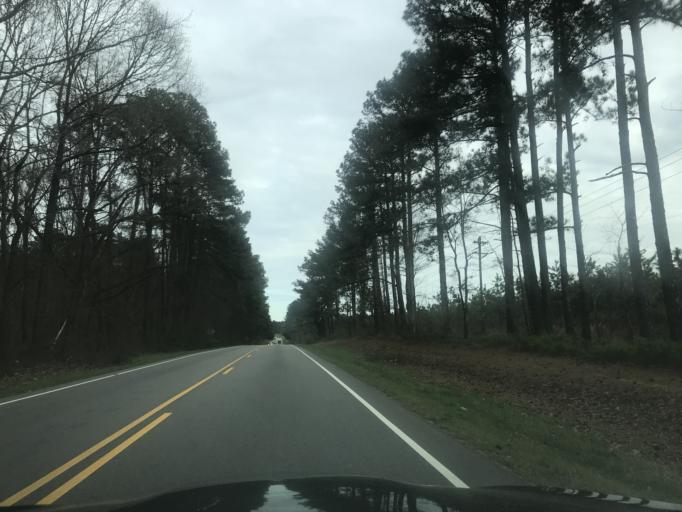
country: US
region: North Carolina
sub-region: Franklin County
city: Franklinton
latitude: 36.1008
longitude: -78.4276
